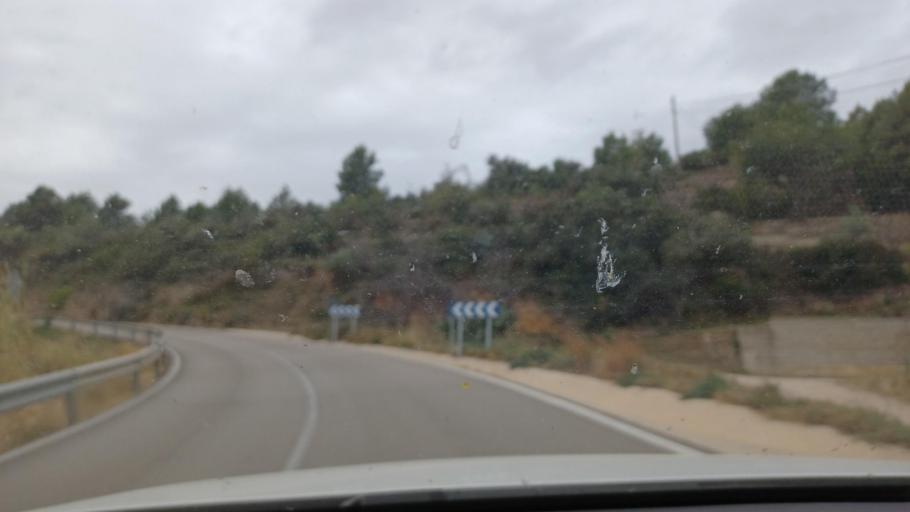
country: ES
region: Valencia
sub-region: Provincia de Castello
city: Rosell
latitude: 40.6328
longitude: 0.2747
